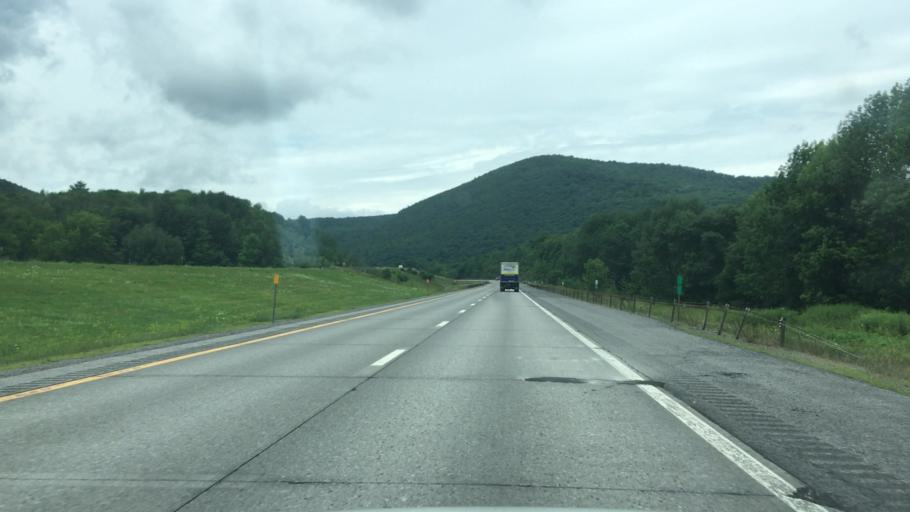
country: US
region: New York
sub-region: Schoharie County
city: Cobleskill
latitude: 42.6493
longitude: -74.6203
